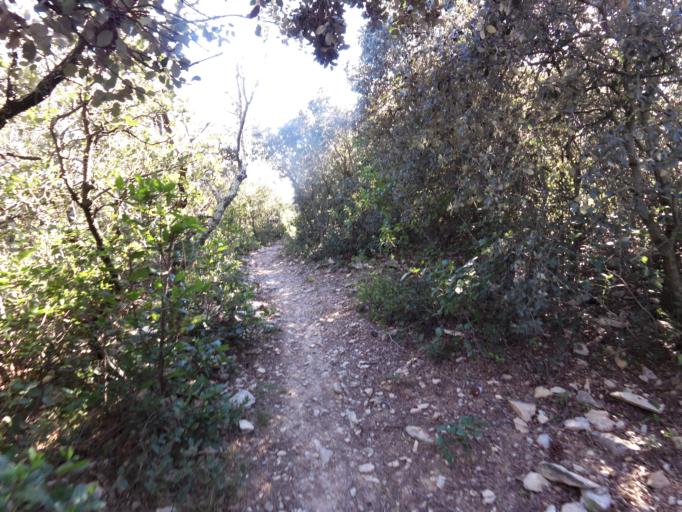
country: FR
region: Languedoc-Roussillon
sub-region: Departement du Gard
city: Clarensac
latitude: 43.8363
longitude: 4.2062
